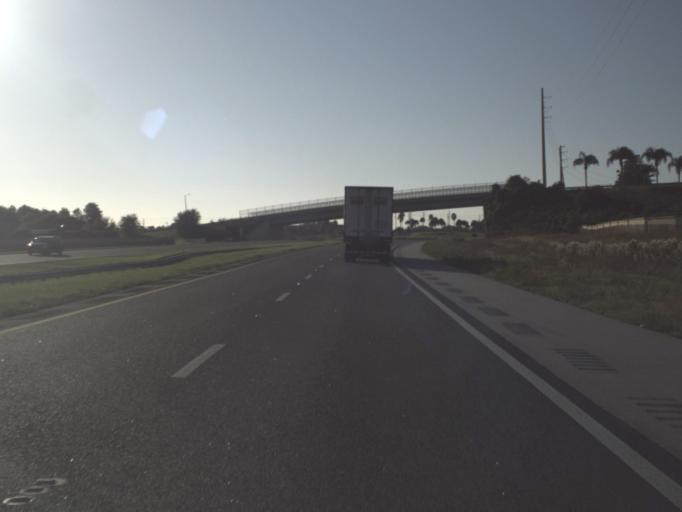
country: US
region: Florida
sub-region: Polk County
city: Citrus Ridge
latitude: 28.3202
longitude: -81.6105
